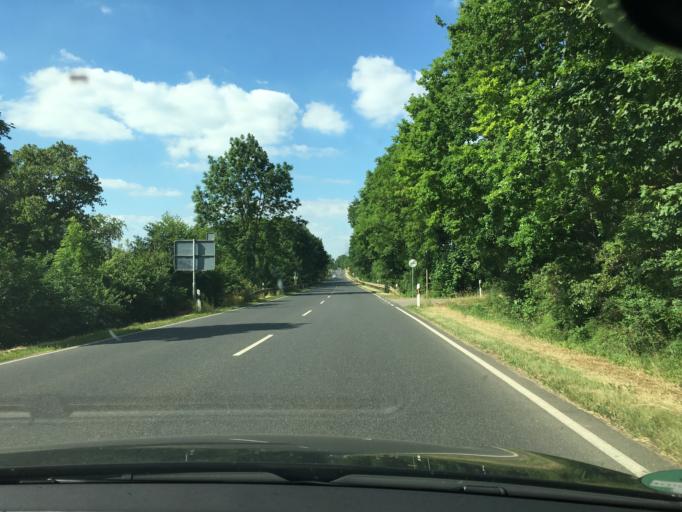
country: DE
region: North Rhine-Westphalia
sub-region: Regierungsbezirk Koln
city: Kreuzau
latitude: 50.7504
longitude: 6.4680
